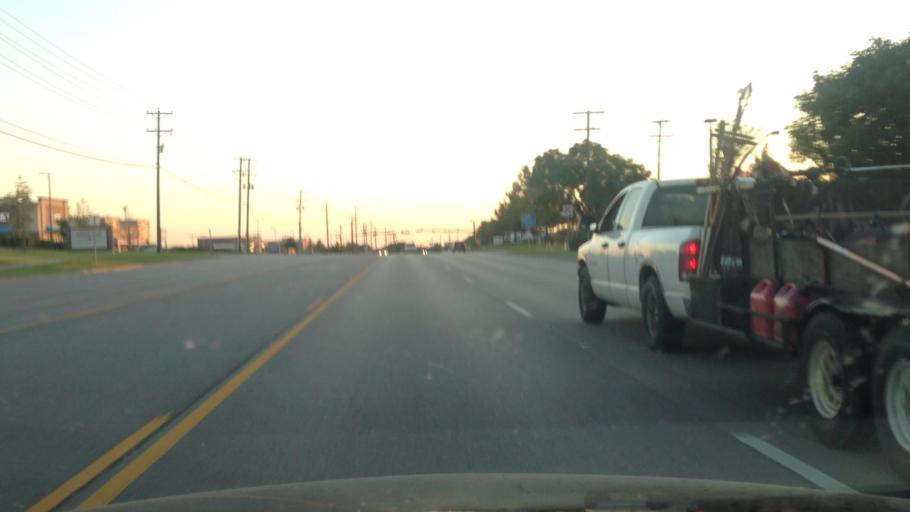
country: US
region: Texas
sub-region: Tarrant County
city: Colleyville
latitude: 32.9066
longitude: -97.1917
